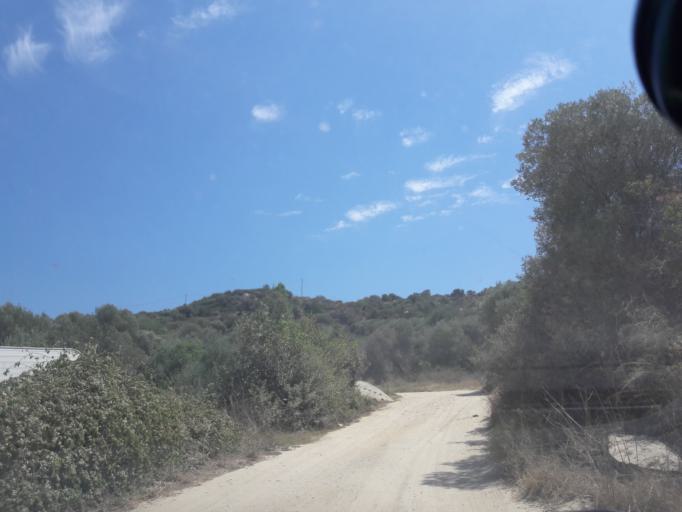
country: GR
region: Central Macedonia
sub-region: Nomos Chalkidikis
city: Ouranoupolis
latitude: 40.3162
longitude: 23.9332
